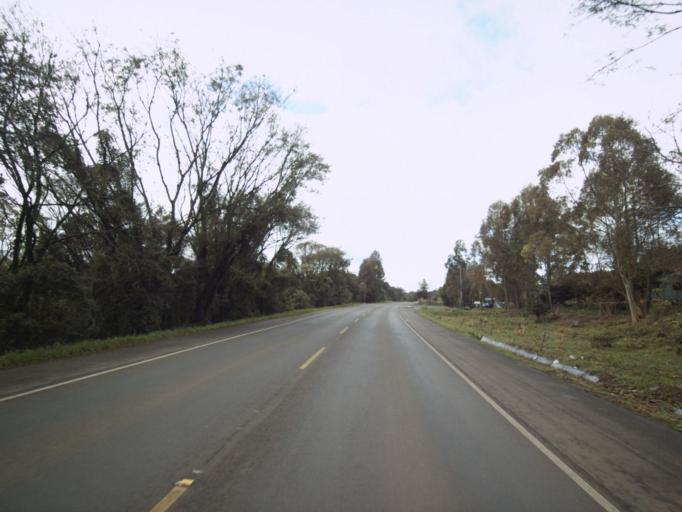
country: BR
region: Santa Catarina
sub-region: Concordia
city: Concordia
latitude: -27.0911
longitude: -51.9061
